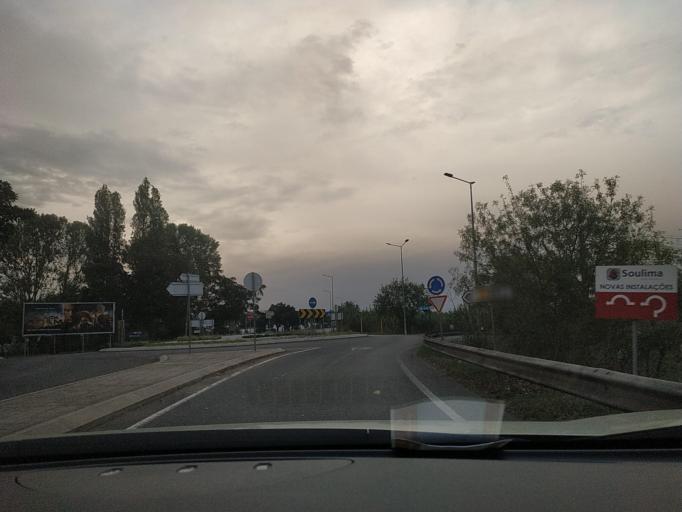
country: PT
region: Lisbon
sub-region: Loures
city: Santa Iria da Azoia
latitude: 38.8659
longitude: -9.0959
